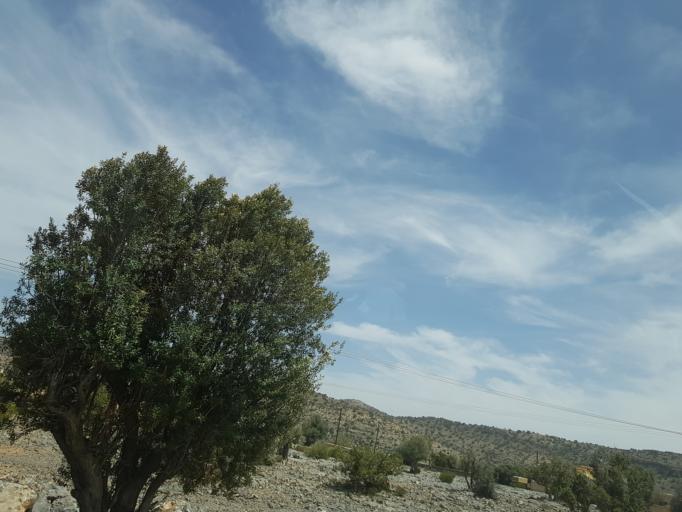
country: OM
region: Al Batinah
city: Bayt al `Awabi
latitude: 23.1370
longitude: 57.5701
